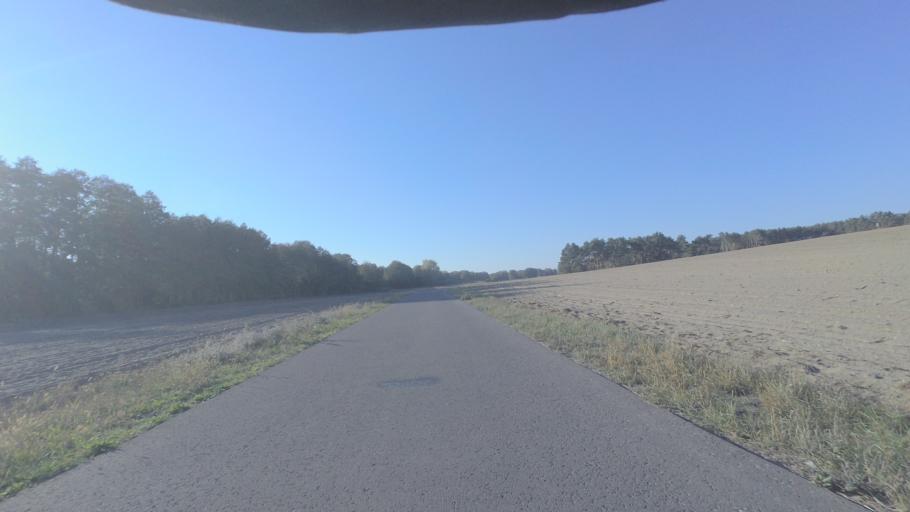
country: DE
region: Brandenburg
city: Mittenwalde
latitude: 52.2532
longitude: 13.5471
